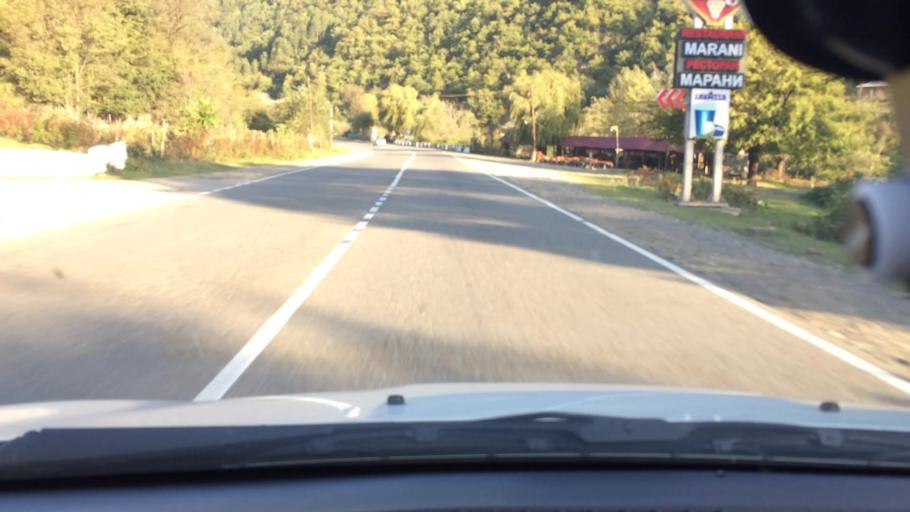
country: GE
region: Imereti
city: Kharagauli
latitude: 42.1062
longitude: 43.3400
